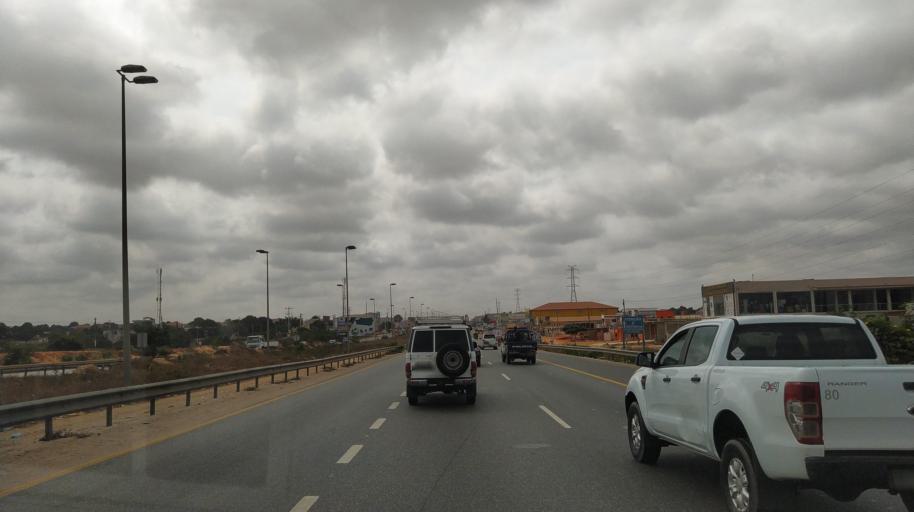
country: AO
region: Luanda
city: Luanda
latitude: -8.9732
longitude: 13.2980
